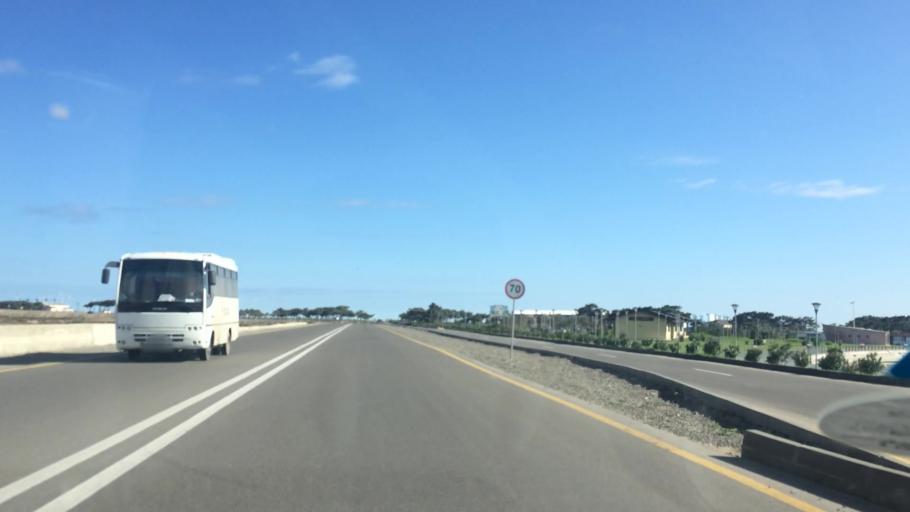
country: AZ
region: Baki
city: Pirallahi
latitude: 40.4090
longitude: 50.3507
